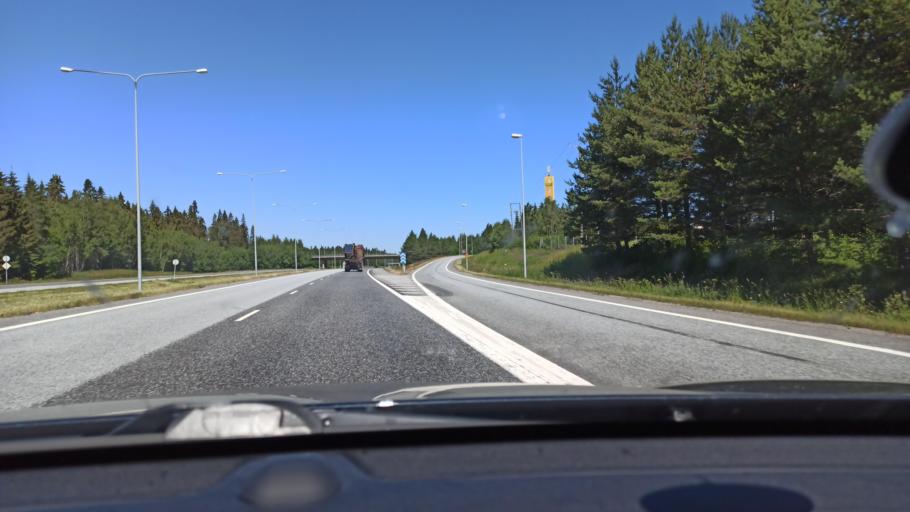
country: FI
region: Ostrobothnia
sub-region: Vaasa
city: Ristinummi
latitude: 63.0509
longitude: 21.7175
